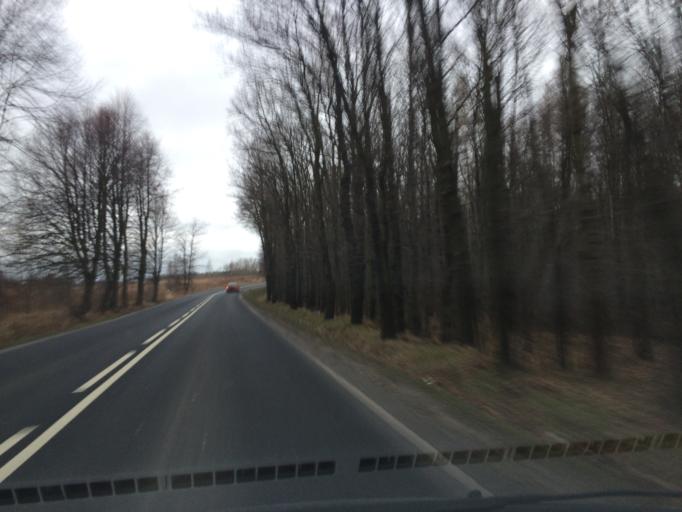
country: PL
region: Lower Silesian Voivodeship
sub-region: Powiat lubanski
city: Luban
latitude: 51.1399
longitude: 15.2732
